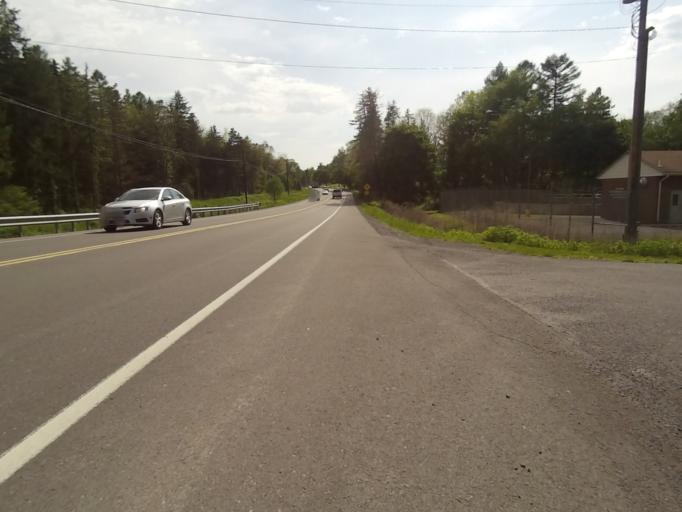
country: US
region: Pennsylvania
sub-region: Centre County
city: Pleasant Gap
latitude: 40.8530
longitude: -77.7695
